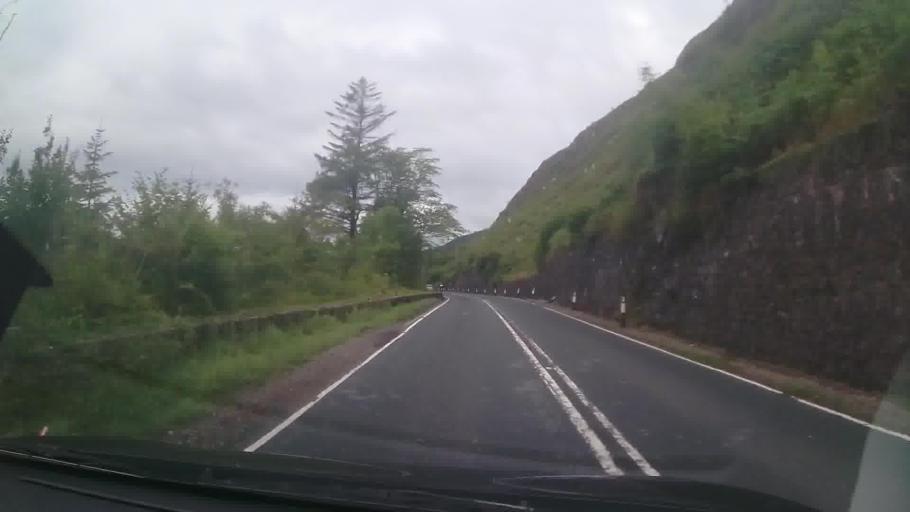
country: GB
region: Scotland
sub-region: Highland
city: Fort William
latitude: 56.7346
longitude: -5.2170
